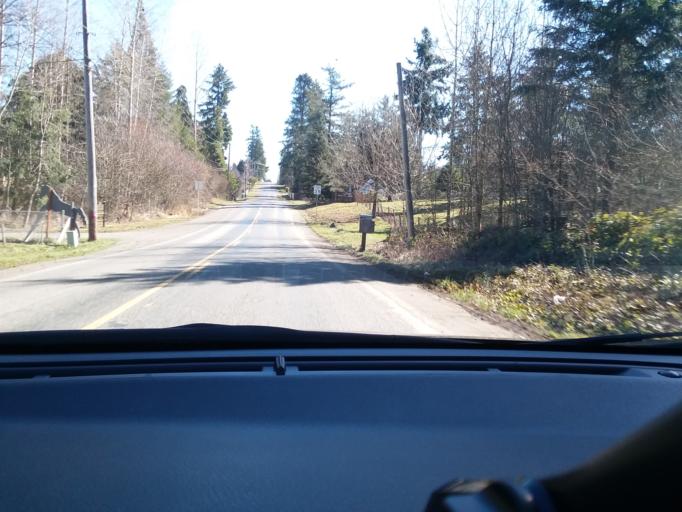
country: US
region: Washington
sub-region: Pierce County
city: Summit
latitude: 47.1699
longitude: -122.3682
